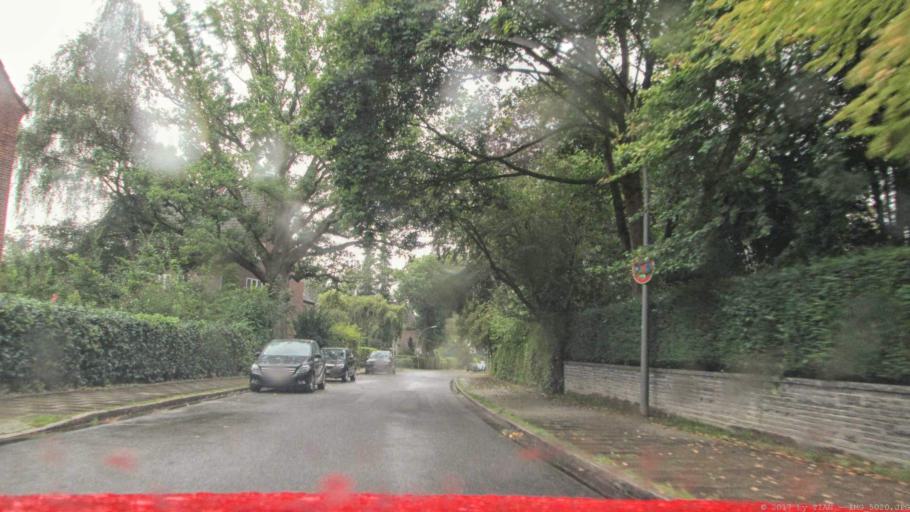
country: DE
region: Schleswig-Holstein
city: Halstenbek
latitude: 53.5577
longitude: 9.8437
